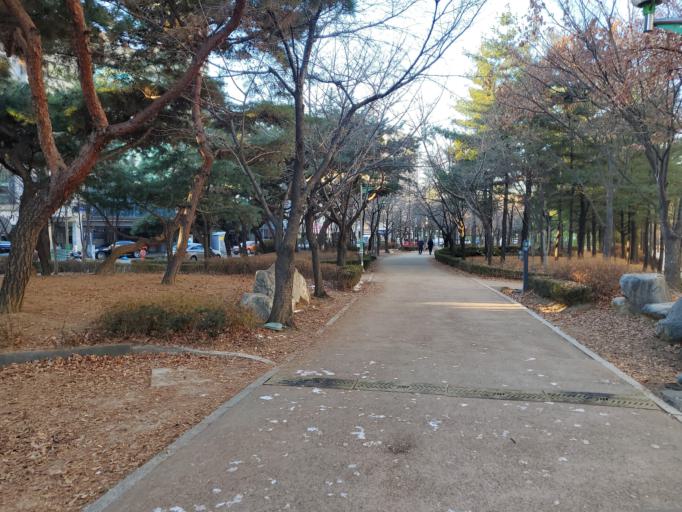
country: KR
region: Gyeonggi-do
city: Seongnam-si
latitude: 37.4866
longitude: 127.1291
